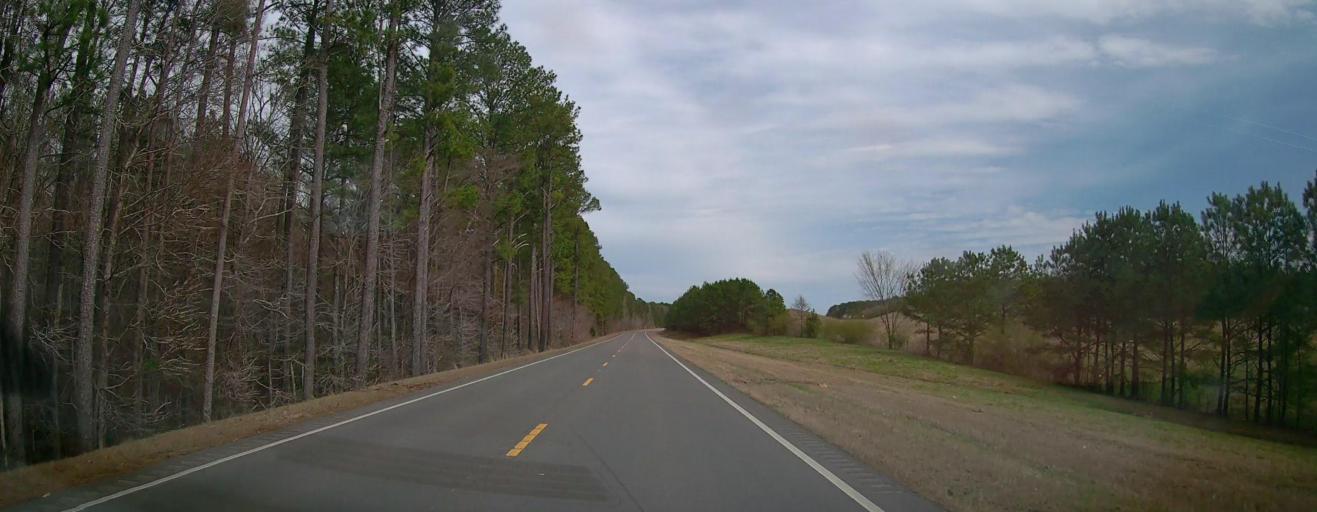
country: US
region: Alabama
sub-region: Walker County
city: Jasper
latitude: 33.8639
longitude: -87.3991
